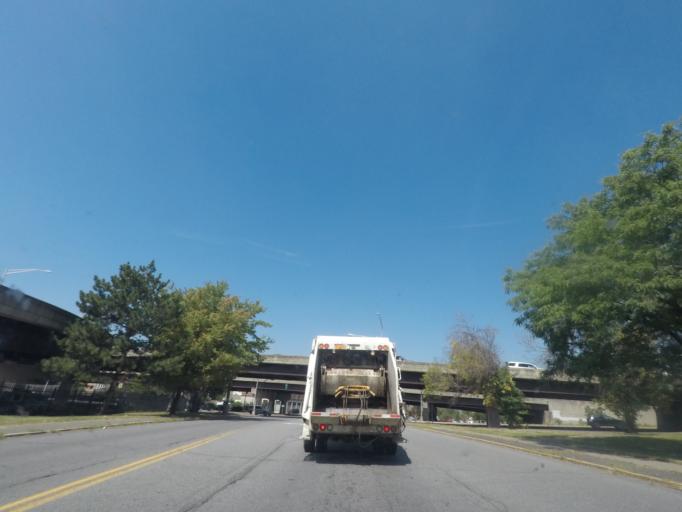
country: US
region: New York
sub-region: Albany County
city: Green Island
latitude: 42.7391
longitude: -73.6828
